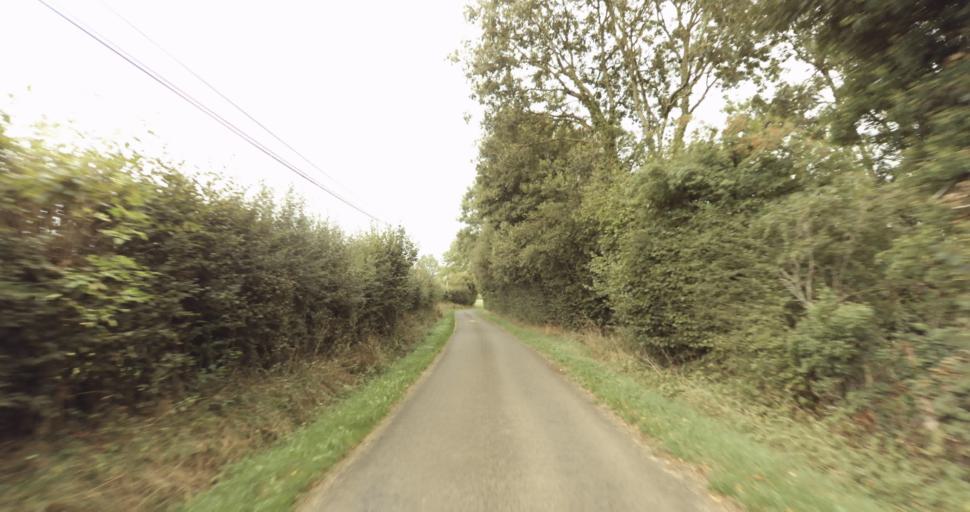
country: FR
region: Lower Normandy
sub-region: Departement de l'Orne
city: Gace
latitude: 48.7251
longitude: 0.3193
